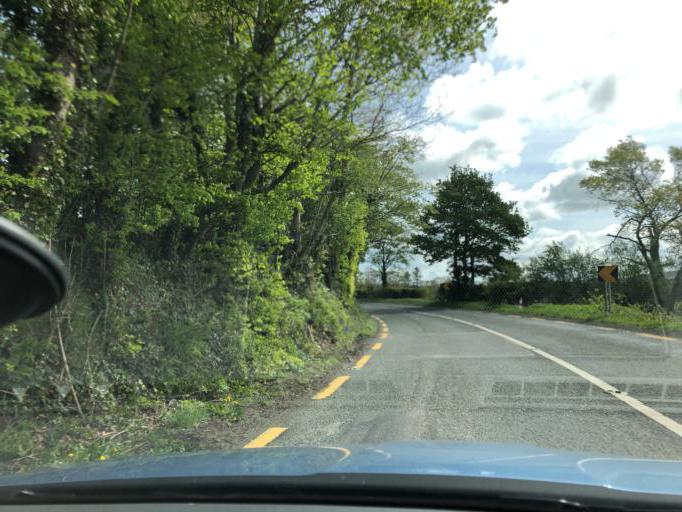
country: IE
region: Munster
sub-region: County Cork
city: Kanturk
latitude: 52.1381
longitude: -8.8956
